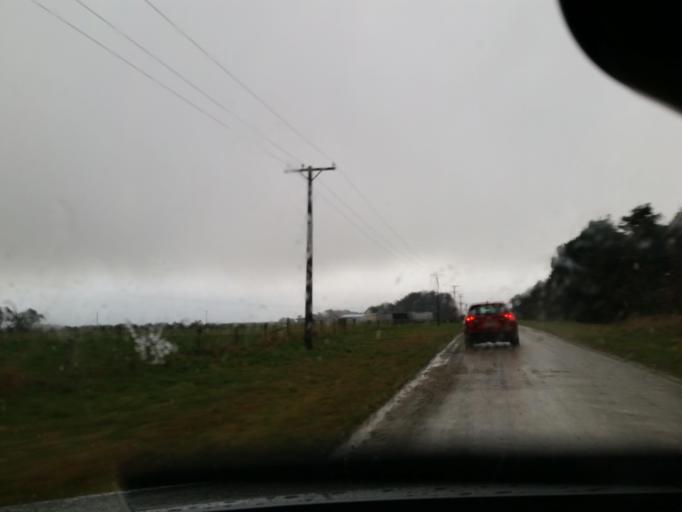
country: NZ
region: Southland
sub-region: Invercargill City
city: Invercargill
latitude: -46.3337
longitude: 168.4534
